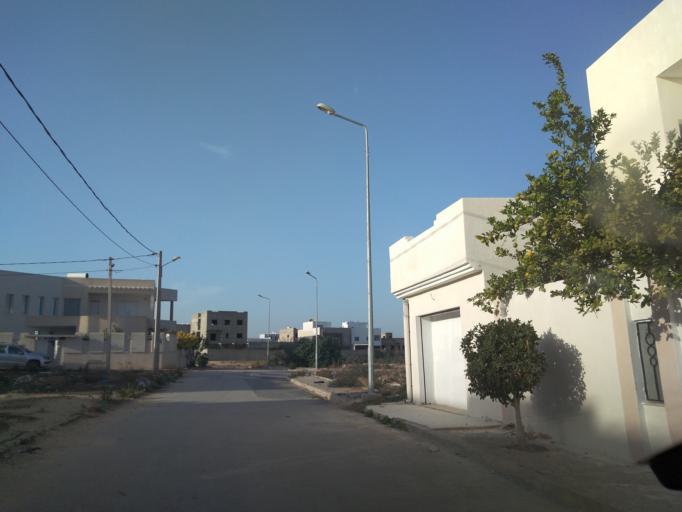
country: TN
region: Manouba
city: Manouba
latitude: 36.7952
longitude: 10.0860
